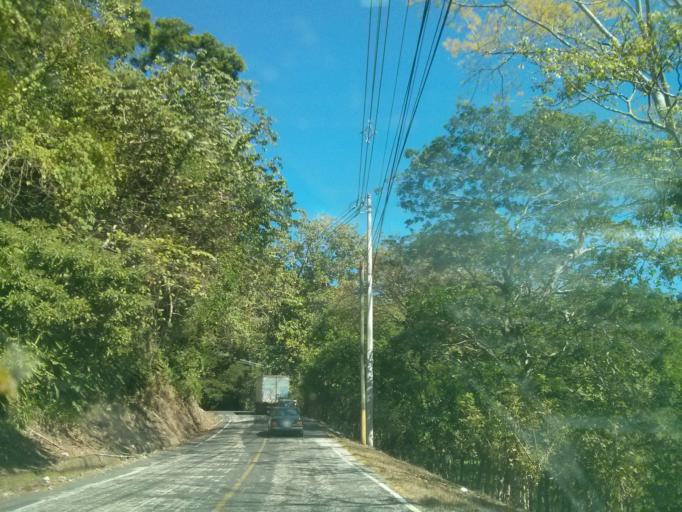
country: CR
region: Puntarenas
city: Paquera
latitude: 9.7889
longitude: -84.9413
